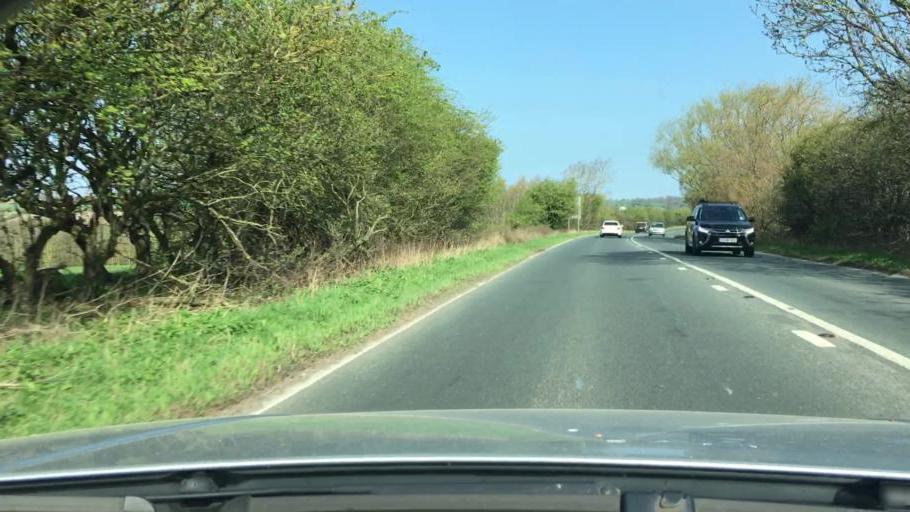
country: GB
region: England
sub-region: North Yorkshire
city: Pannal
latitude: 53.9407
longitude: -1.5372
